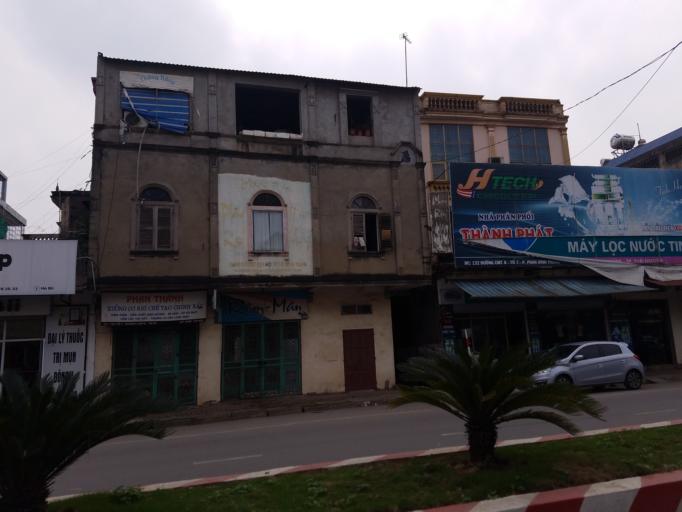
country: VN
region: Thai Nguyen
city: Thanh Pho Thai Nguyen
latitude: 21.5912
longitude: 105.8450
